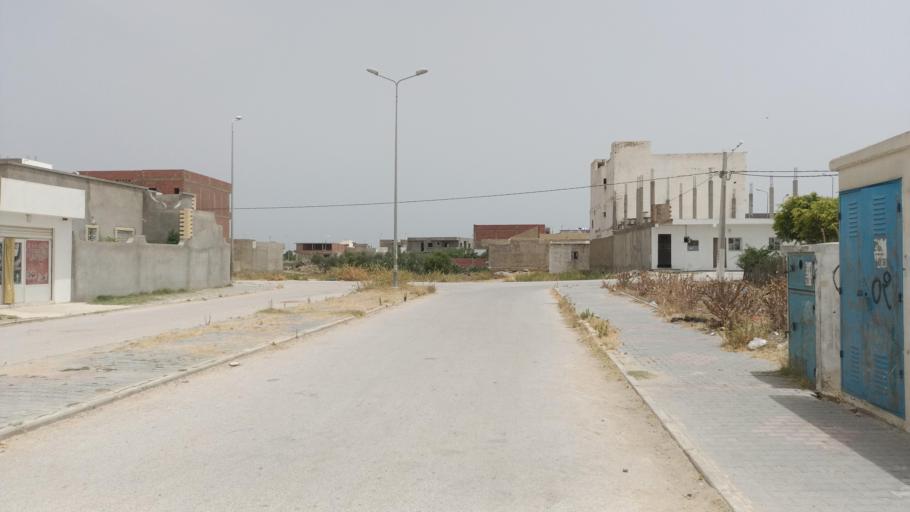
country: TN
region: Nabul
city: Manzil Bu Zalafah
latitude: 36.7042
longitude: 10.4907
